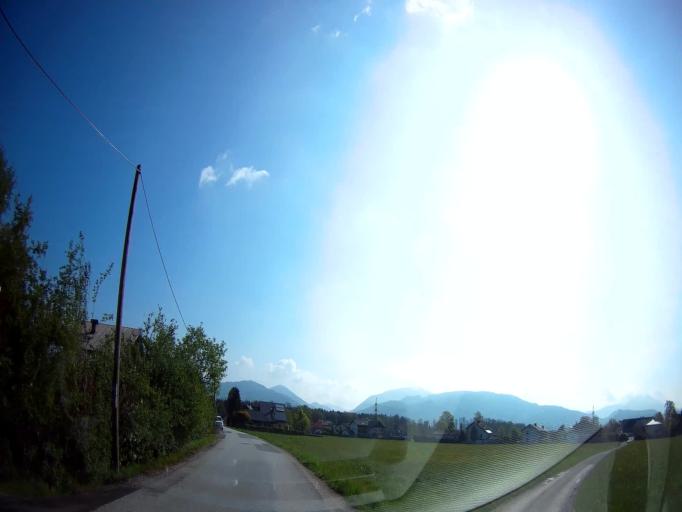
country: AT
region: Salzburg
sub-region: Politischer Bezirk Salzburg-Umgebung
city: Grodig
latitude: 47.7529
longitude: 13.0317
